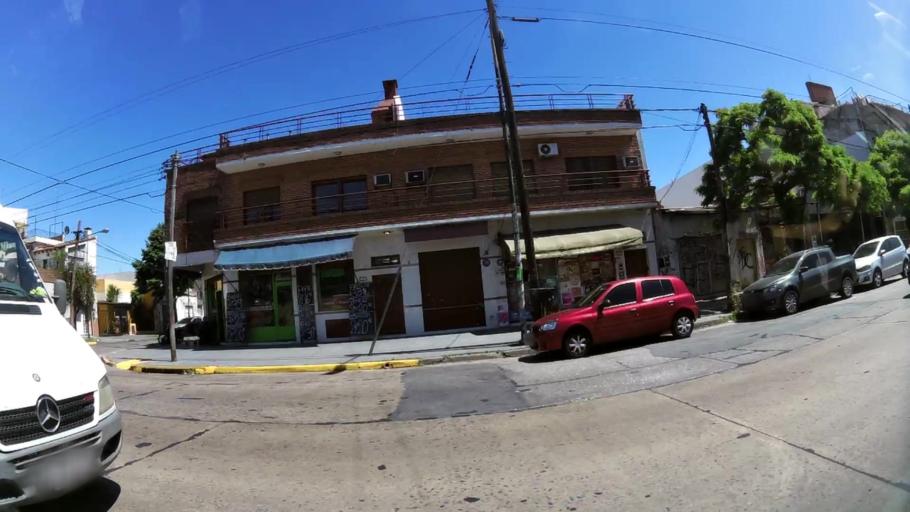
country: AR
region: Buenos Aires
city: Caseros
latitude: -34.5885
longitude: -58.5627
